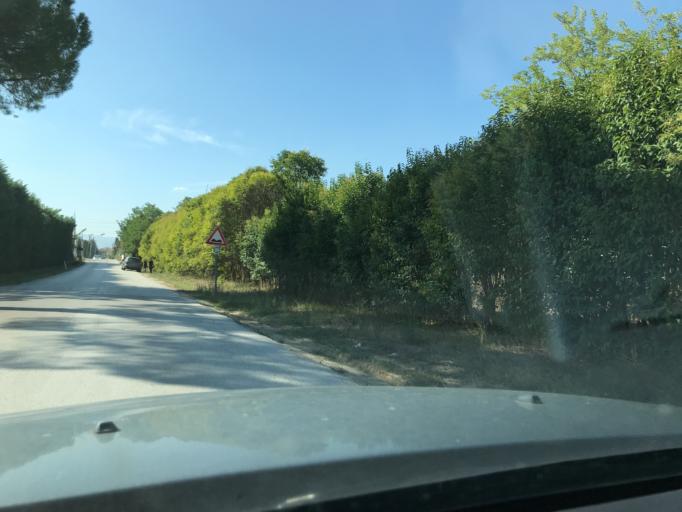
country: IT
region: Umbria
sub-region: Provincia di Perugia
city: Ospedalicchio
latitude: 43.0837
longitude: 12.5067
